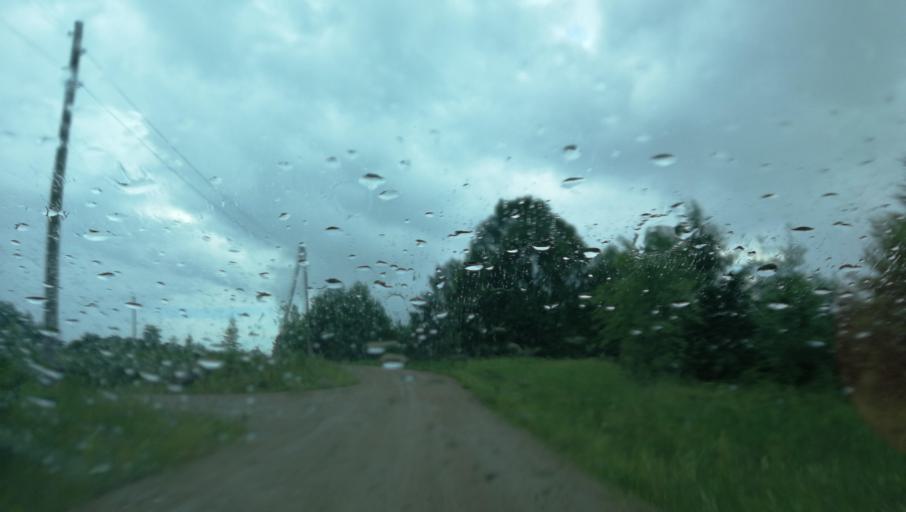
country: LV
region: Vecpiebalga
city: Vecpiebalga
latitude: 57.1005
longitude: 25.6909
